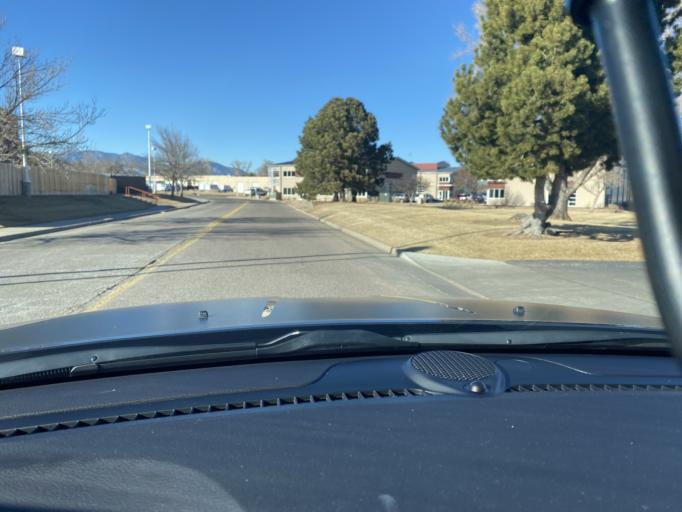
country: US
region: Colorado
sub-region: Jefferson County
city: Applewood
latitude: 39.8145
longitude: -105.1619
